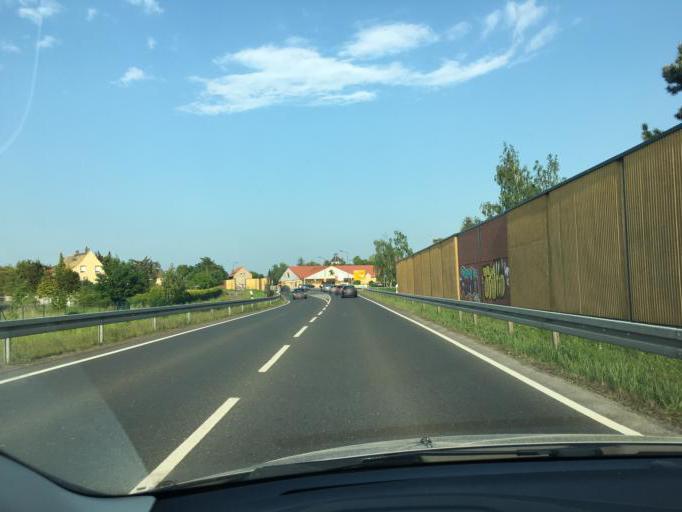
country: DE
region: Saxony
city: Grimma
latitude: 51.2521
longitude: 12.7236
